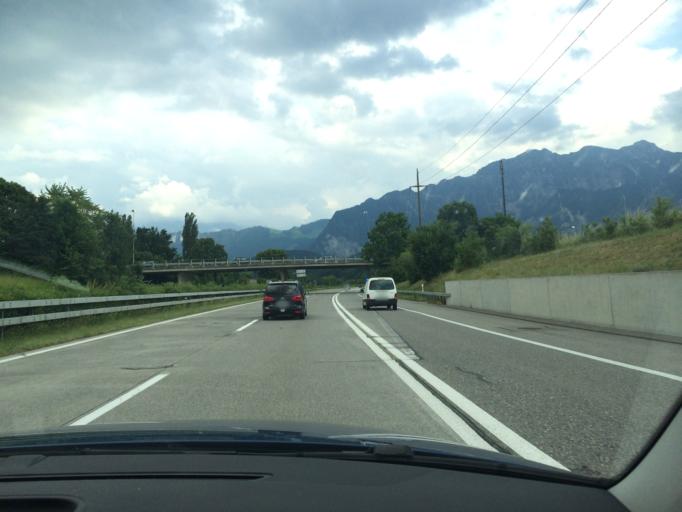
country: CH
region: Bern
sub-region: Thun District
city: Thun
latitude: 46.7440
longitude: 7.6028
